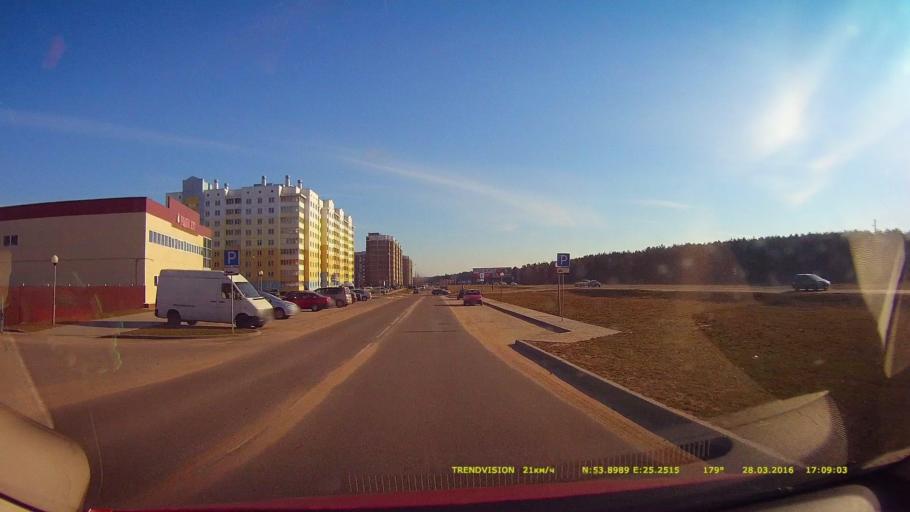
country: BY
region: Grodnenskaya
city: Lida
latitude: 53.8987
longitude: 25.2515
